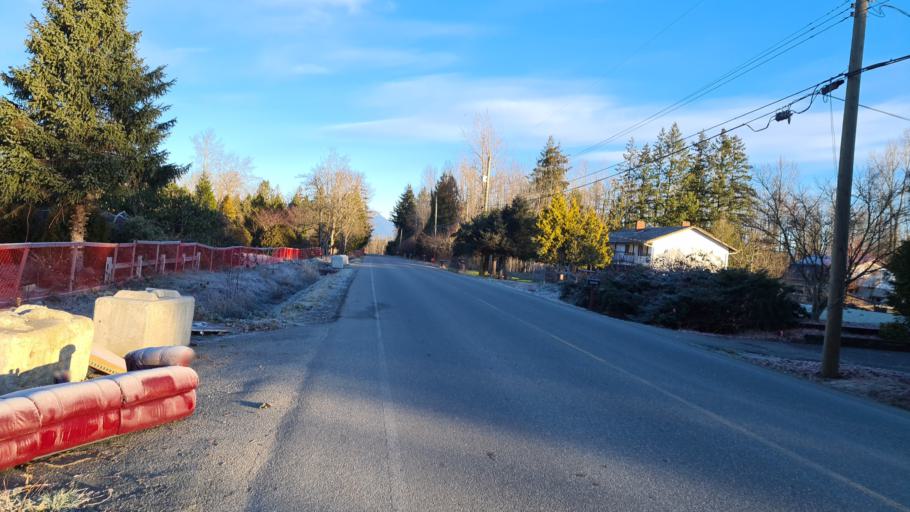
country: CA
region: British Columbia
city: Langley
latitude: 49.1362
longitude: -122.6723
